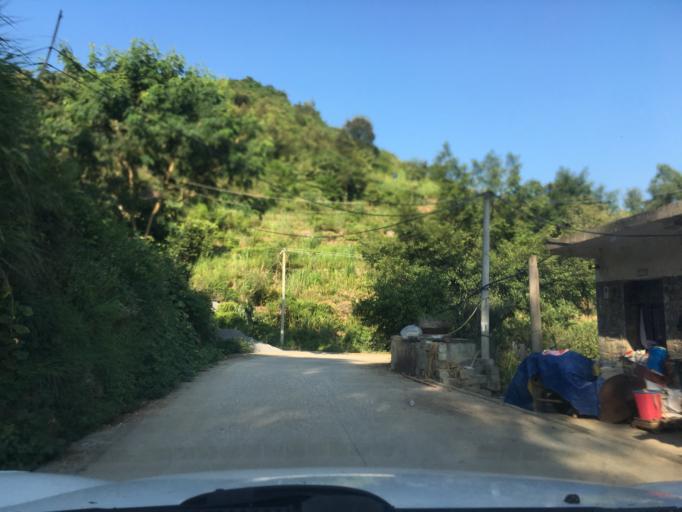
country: CN
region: Guangxi Zhuangzu Zizhiqu
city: Xinzhou
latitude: 25.3909
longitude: 105.7686
